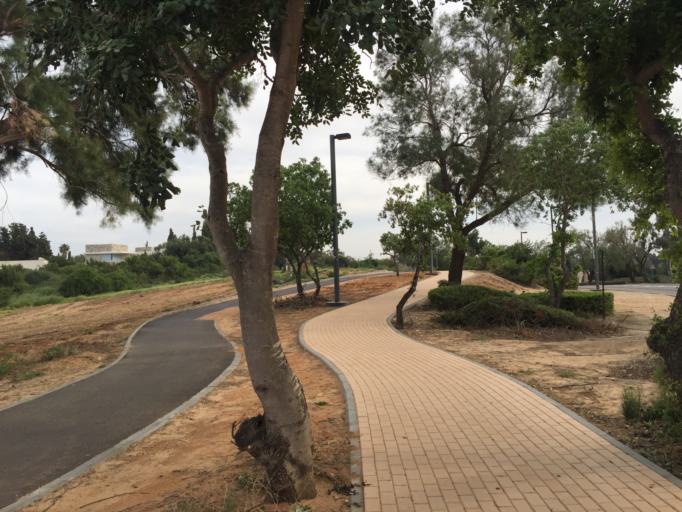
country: IL
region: Haifa
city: Qesarya
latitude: 32.5070
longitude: 34.9038
